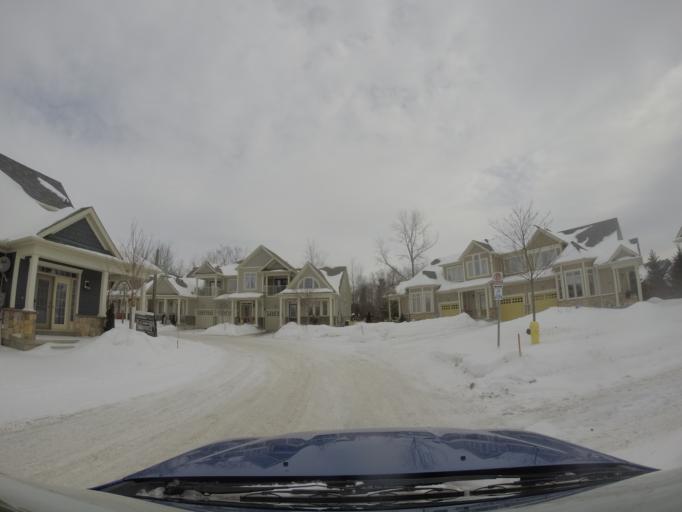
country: CA
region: Ontario
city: Wasaga Beach
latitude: 44.5280
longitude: -80.0066
